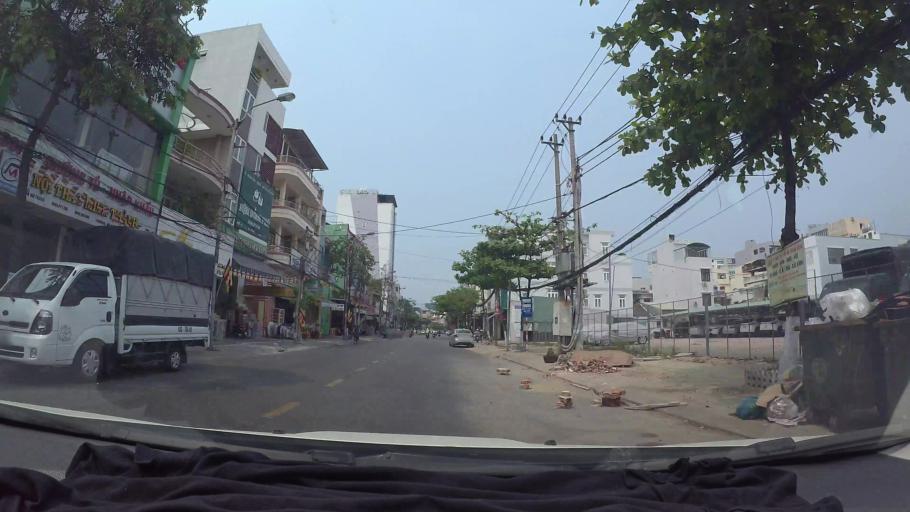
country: VN
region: Da Nang
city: Son Tra
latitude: 16.0529
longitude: 108.2203
